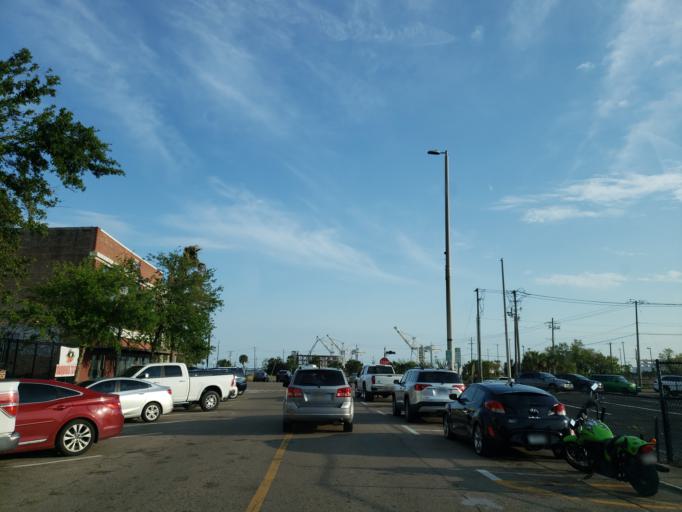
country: US
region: Mississippi
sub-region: Harrison County
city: Gulfport
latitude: 30.3677
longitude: -89.0948
